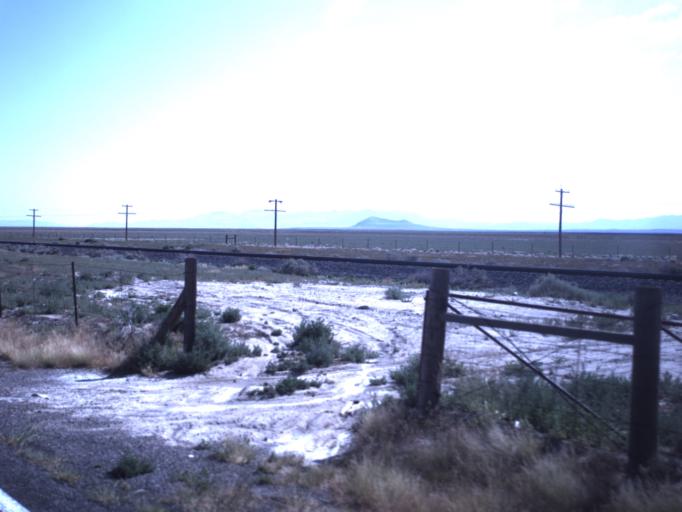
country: US
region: Utah
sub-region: Millard County
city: Delta
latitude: 39.0147
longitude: -112.7817
